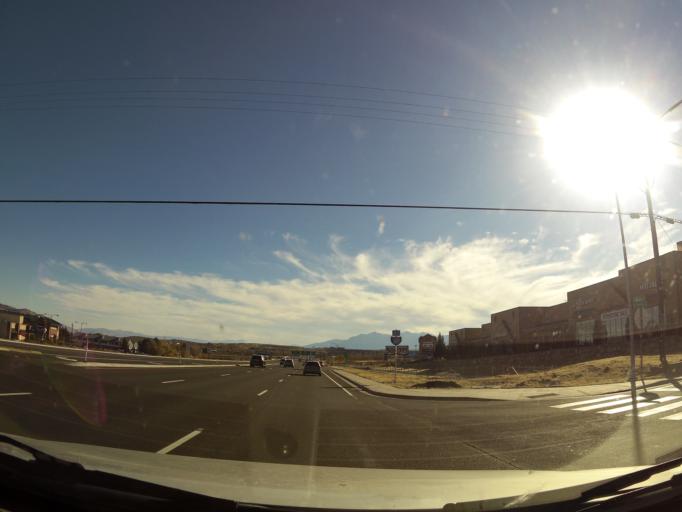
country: US
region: Nevada
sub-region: Carson City
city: Carson City
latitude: 39.1268
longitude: -119.7711
